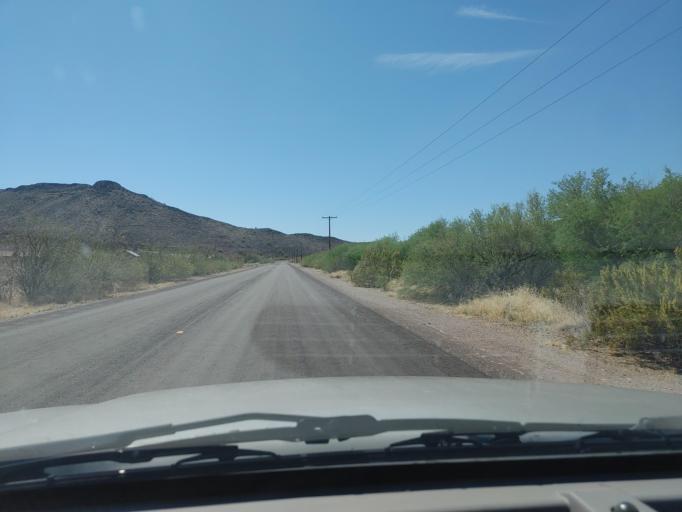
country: US
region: Arizona
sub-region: Maricopa County
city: Gila Bend
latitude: 33.0067
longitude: -113.3404
